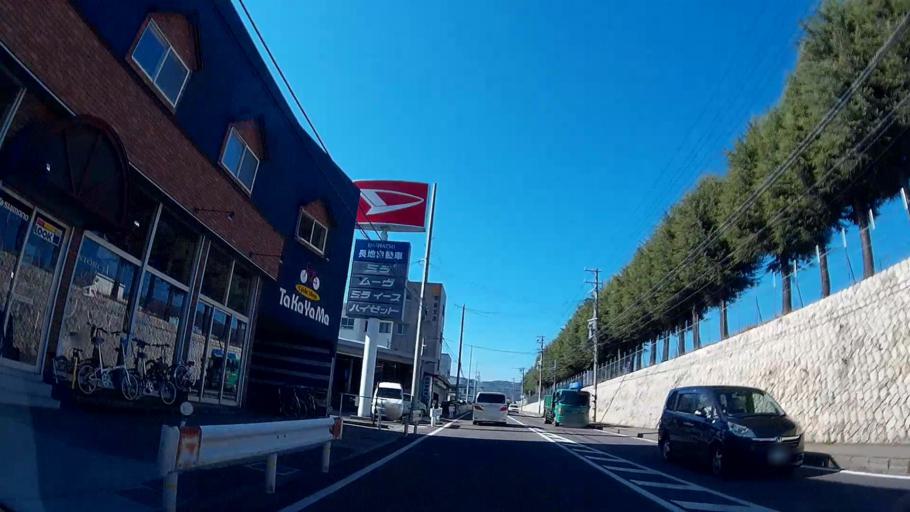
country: JP
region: Nagano
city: Okaya
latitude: 36.0784
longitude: 138.0649
